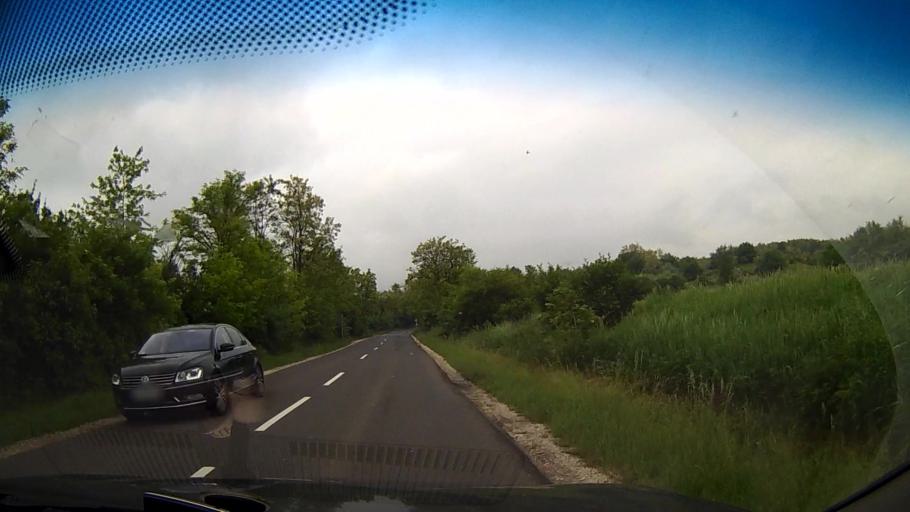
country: HU
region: Pest
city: Piliscsaba
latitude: 47.6413
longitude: 18.7841
